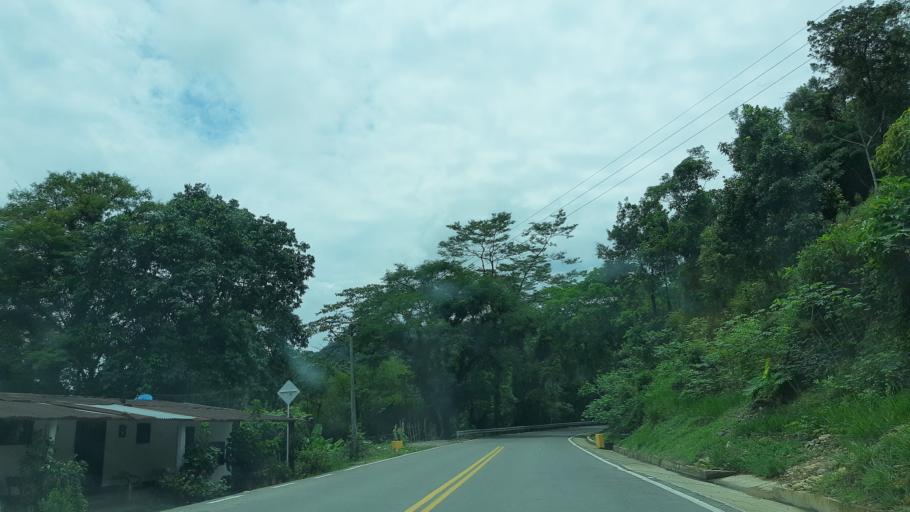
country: CO
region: Boyaca
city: San Luis de Gaceno
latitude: 4.8307
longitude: -73.1328
